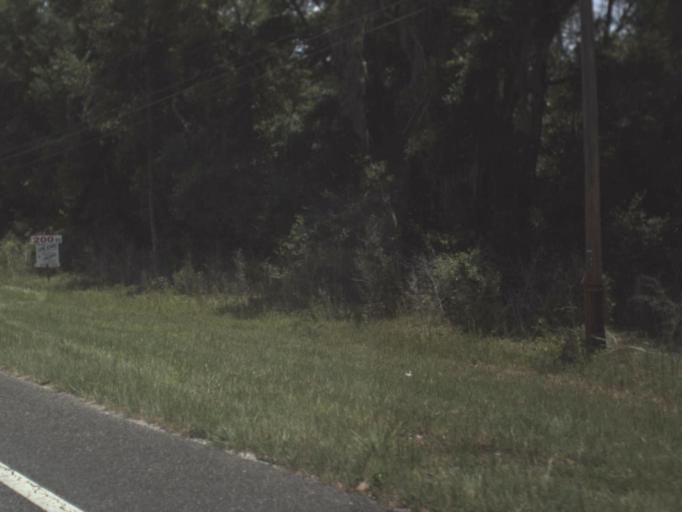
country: US
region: Florida
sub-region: Dixie County
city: Cross City
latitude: 29.6096
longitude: -83.0784
